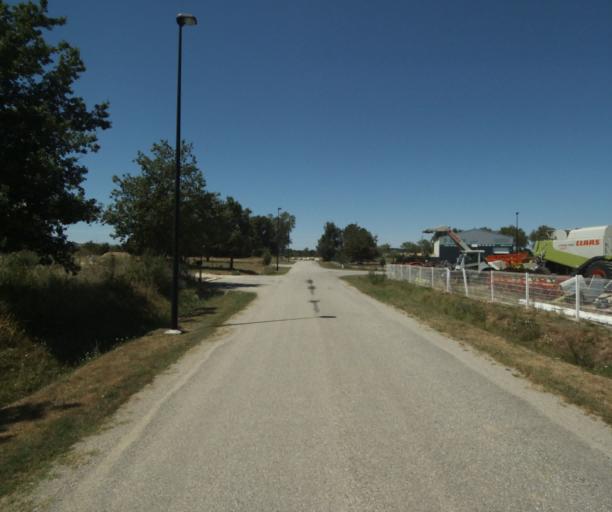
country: FR
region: Midi-Pyrenees
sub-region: Departement de la Haute-Garonne
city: Saint-Felix-Lauragais
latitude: 43.4449
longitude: 1.9420
